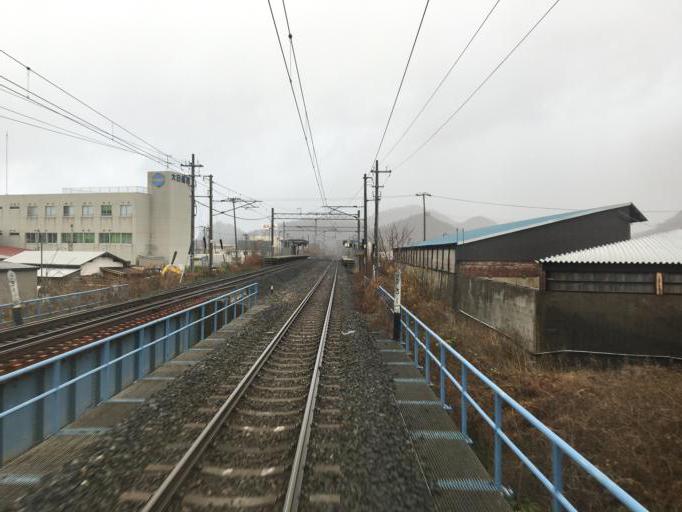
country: JP
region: Aomori
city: Aomori Shi
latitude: 40.8452
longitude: 140.8158
